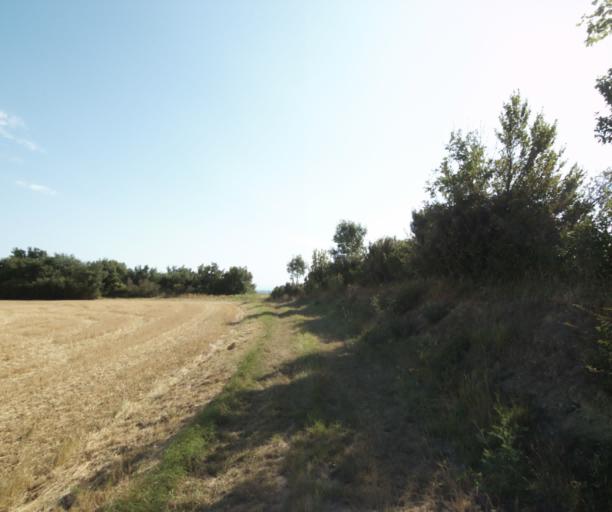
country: FR
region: Midi-Pyrenees
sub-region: Departement de la Haute-Garonne
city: Avignonet-Lauragais
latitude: 43.4160
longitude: 1.8154
